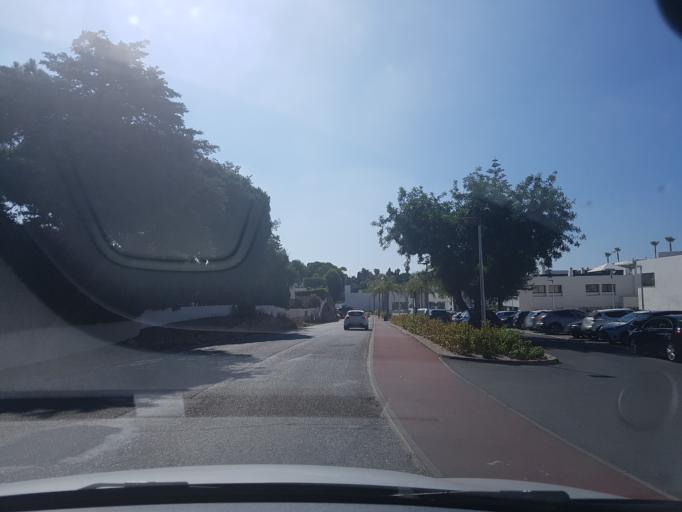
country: PT
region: Faro
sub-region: Lagoa
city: Carvoeiro
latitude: 37.0949
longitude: -8.4611
